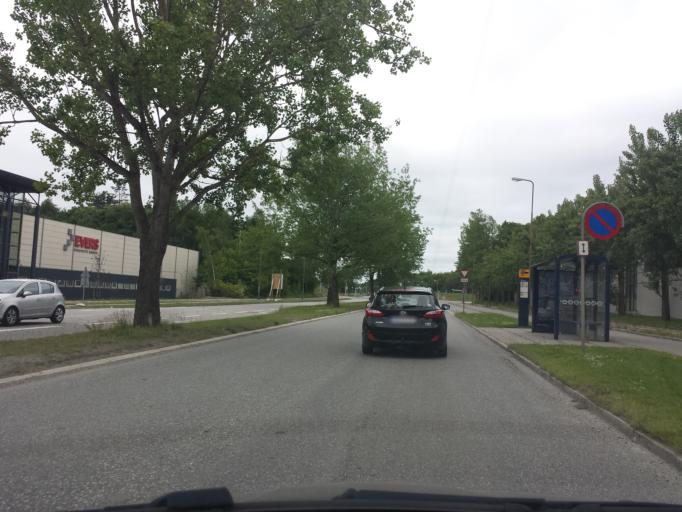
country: DK
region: Capital Region
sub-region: Glostrup Kommune
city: Glostrup
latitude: 55.6939
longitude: 12.4209
